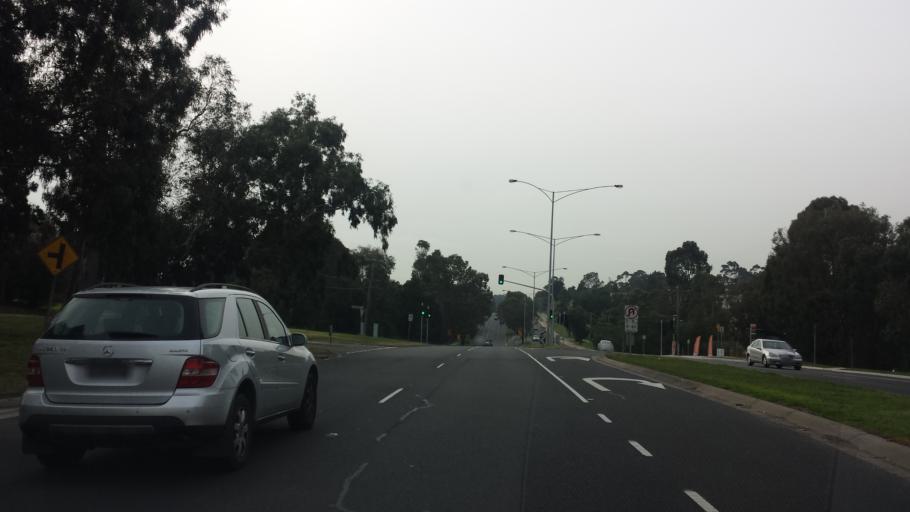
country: AU
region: Victoria
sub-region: Banyule
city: Darch
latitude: -37.7512
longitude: 145.1352
